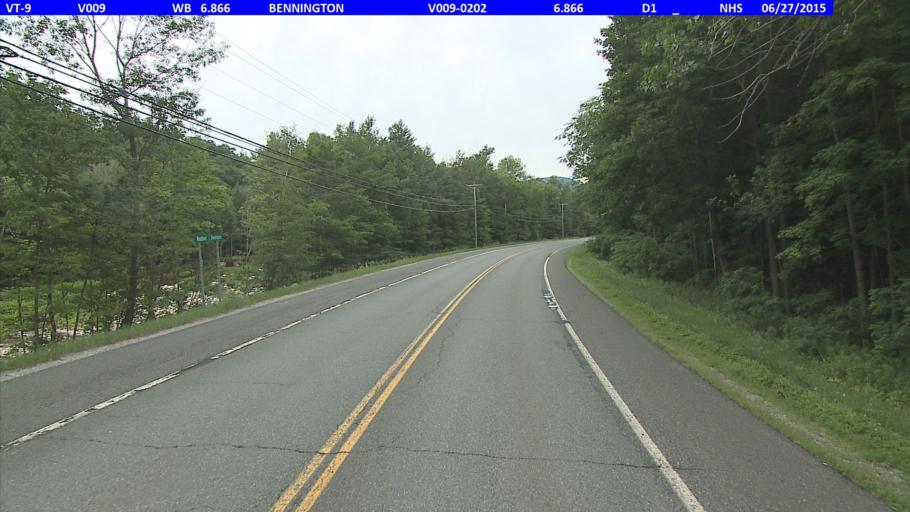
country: US
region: Vermont
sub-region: Bennington County
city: Bennington
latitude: 42.8832
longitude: -73.1499
